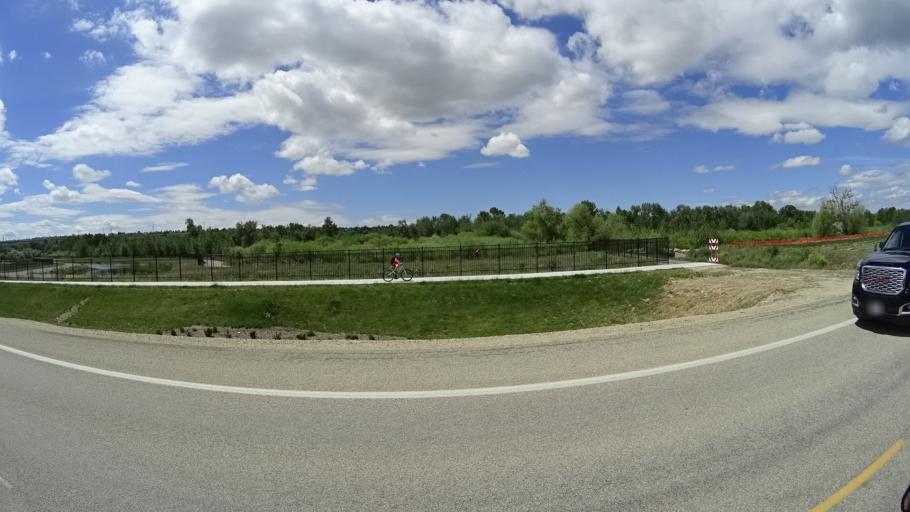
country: US
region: Idaho
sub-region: Ada County
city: Boise
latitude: 43.5700
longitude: -116.1320
